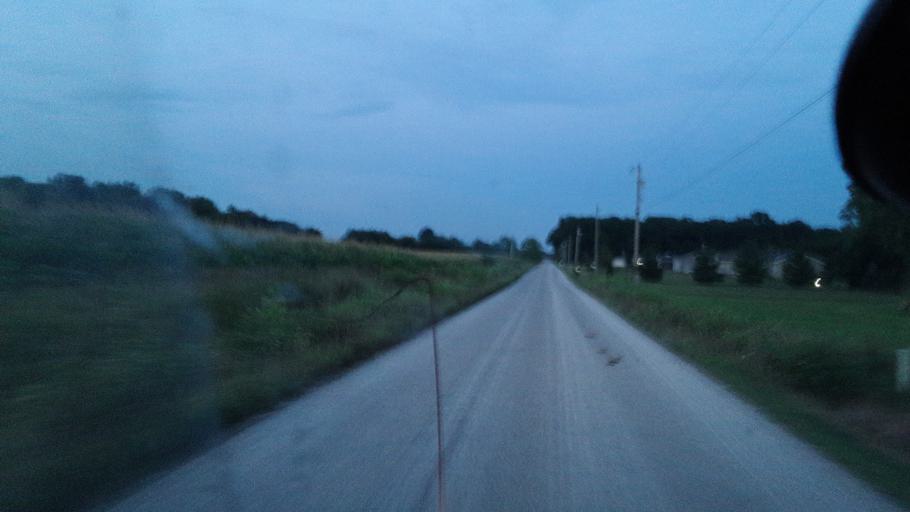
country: US
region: Ohio
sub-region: Wayne County
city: West Salem
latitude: 41.0135
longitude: -82.1974
